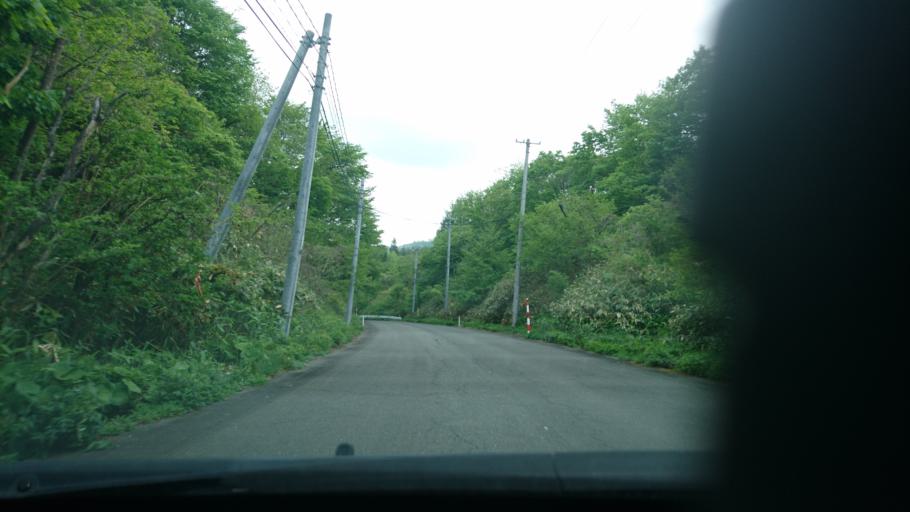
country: JP
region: Iwate
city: Ichinoseki
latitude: 38.8997
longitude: 140.9102
